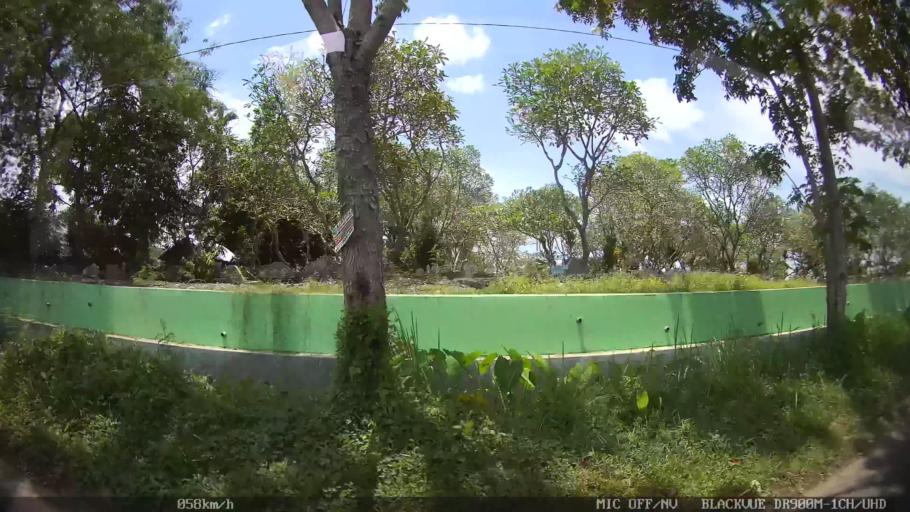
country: ID
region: North Sumatra
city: Binjai
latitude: 3.5912
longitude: 98.5225
